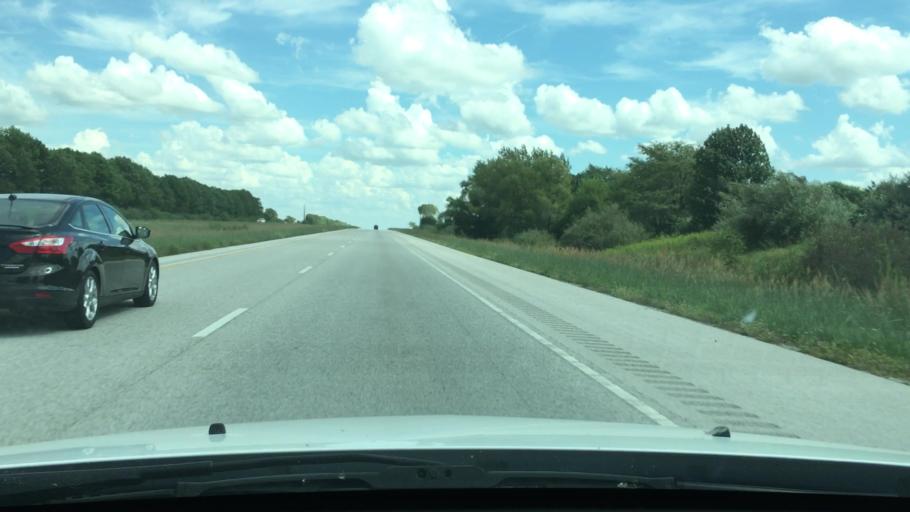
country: US
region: Illinois
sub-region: Scott County
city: Winchester
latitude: 39.6801
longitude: -90.3835
